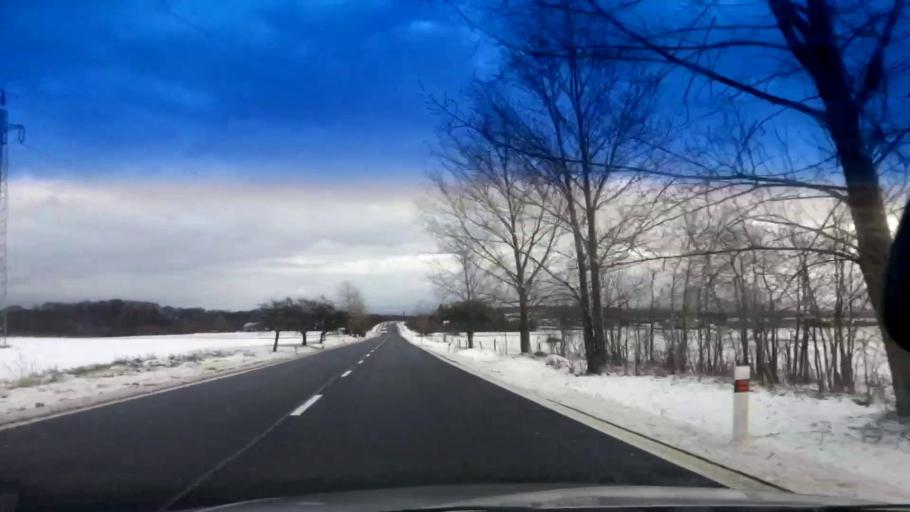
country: CZ
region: Karlovarsky
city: Hazlov
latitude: 50.1691
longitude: 12.2634
